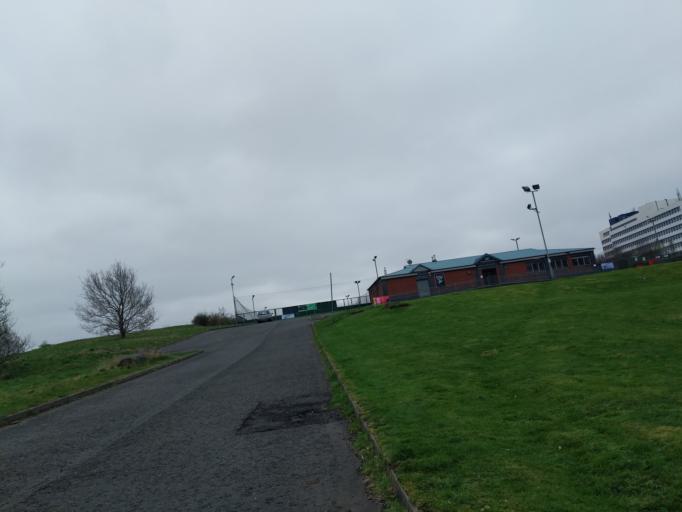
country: GB
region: Scotland
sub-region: Edinburgh
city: Currie
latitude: 55.9285
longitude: -3.2880
